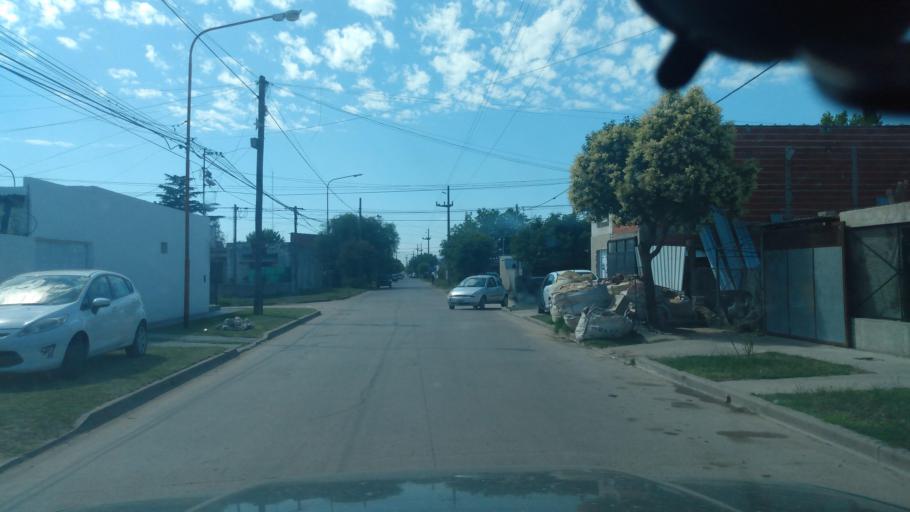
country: AR
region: Buenos Aires
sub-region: Partido de Lujan
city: Lujan
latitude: -34.5774
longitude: -59.1232
